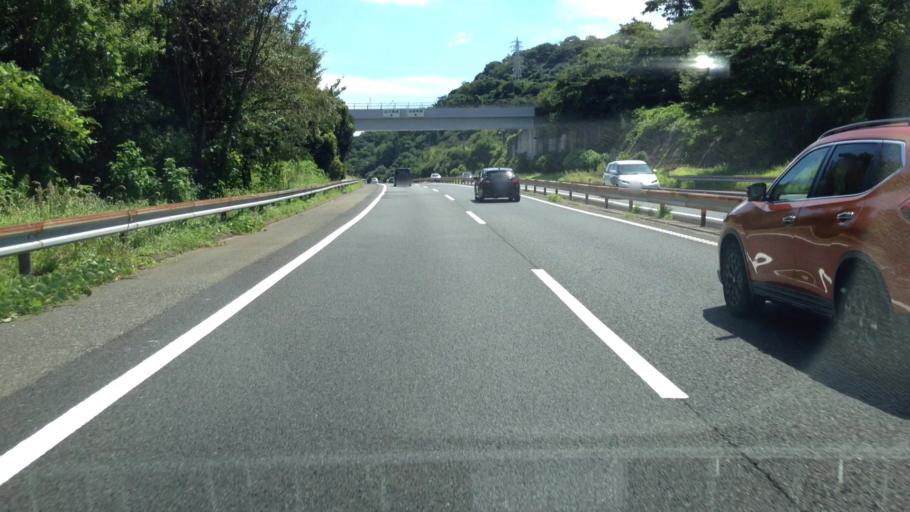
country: JP
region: Kanagawa
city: Yokosuka
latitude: 35.2601
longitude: 139.6337
